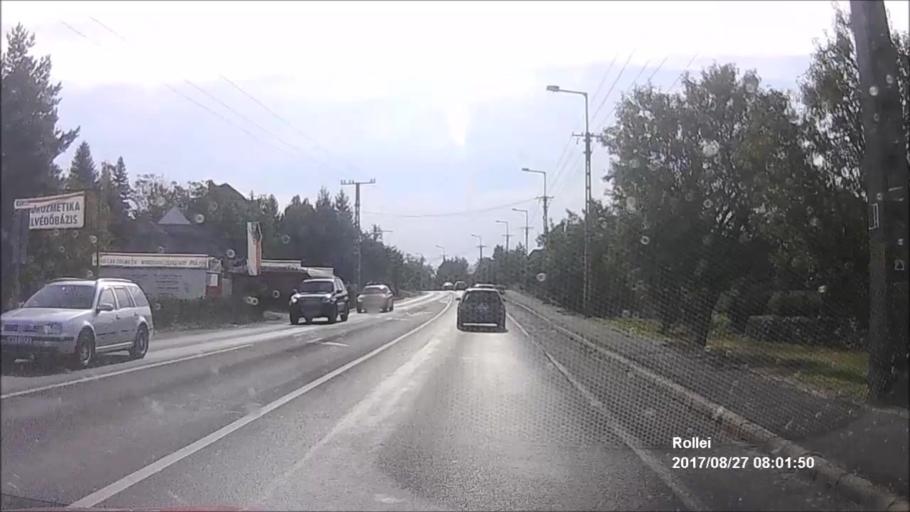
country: HU
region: Zala
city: Vonyarcvashegy
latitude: 46.7620
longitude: 17.3155
